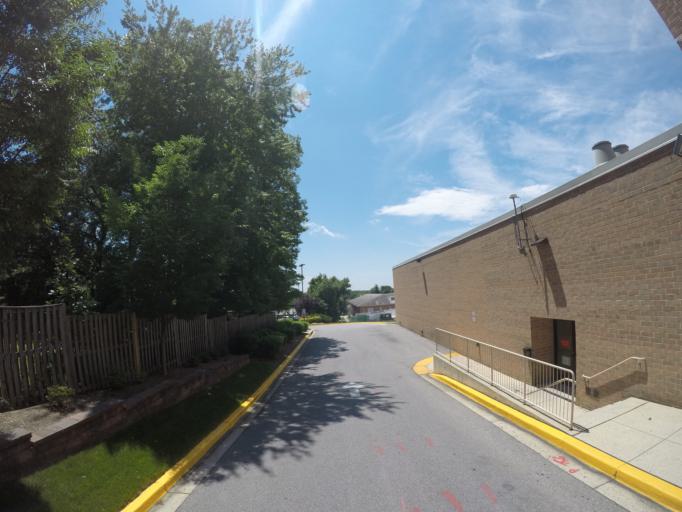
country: US
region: Maryland
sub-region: Prince George's County
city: Goddard
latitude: 38.9824
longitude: -76.8646
